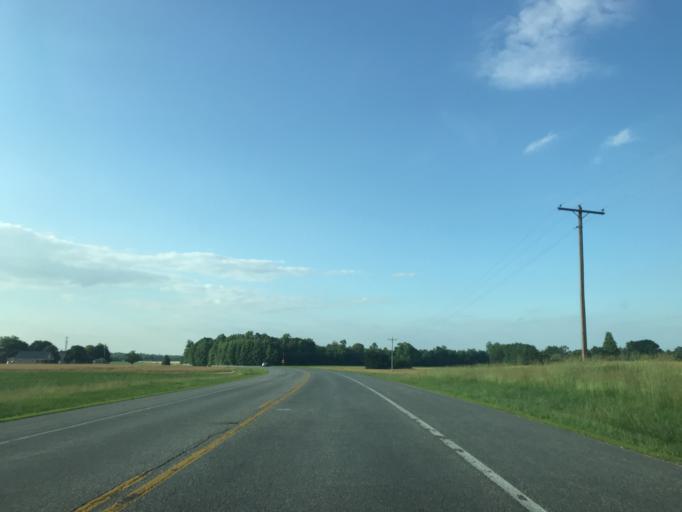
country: US
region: Maryland
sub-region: Caroline County
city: Denton
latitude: 38.8216
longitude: -75.7783
